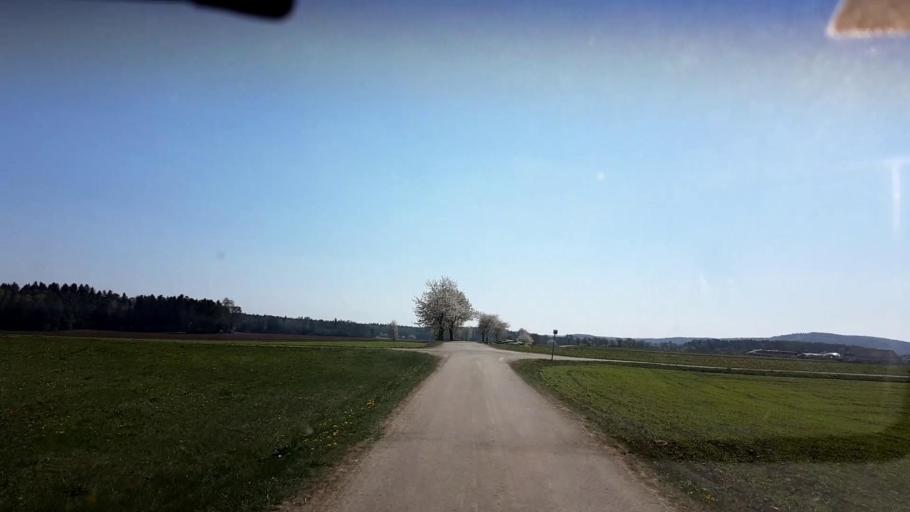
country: DE
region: Bavaria
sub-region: Upper Franconia
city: Heiligenstadt
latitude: 49.9023
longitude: 11.1749
